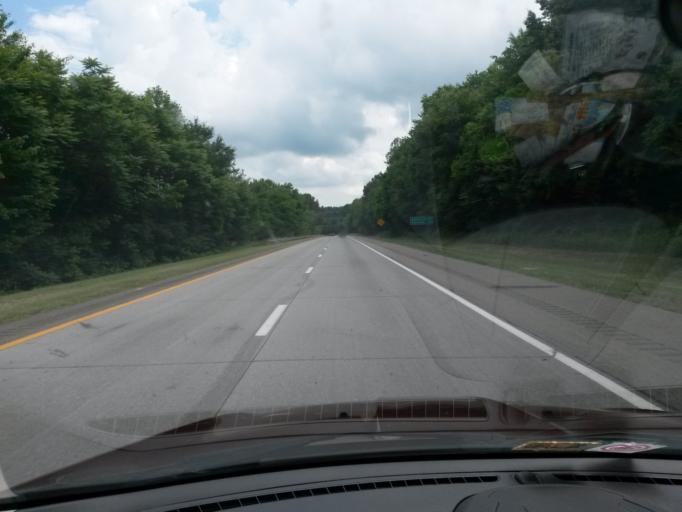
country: US
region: North Carolina
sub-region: Surry County
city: Elkin
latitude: 36.2684
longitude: -80.8257
